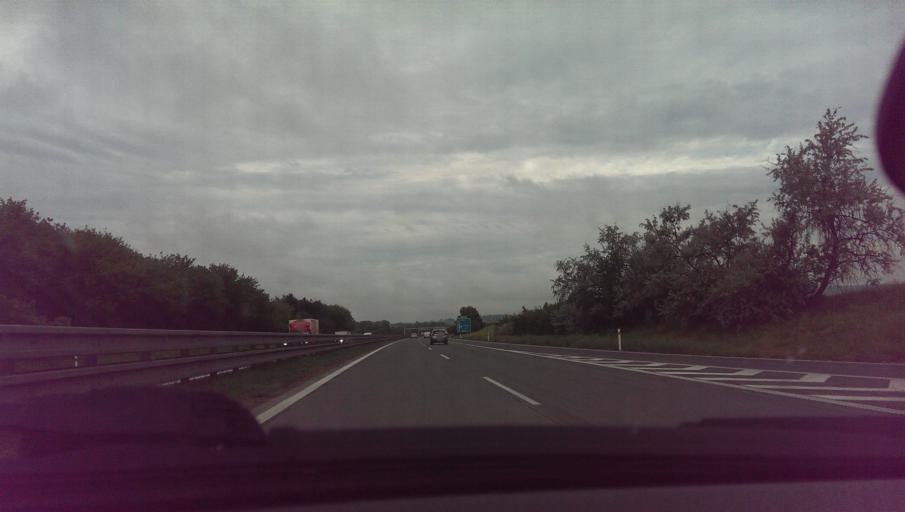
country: CZ
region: South Moravian
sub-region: Okres Vyskov
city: Vyskov
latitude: 49.2588
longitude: 16.9894
